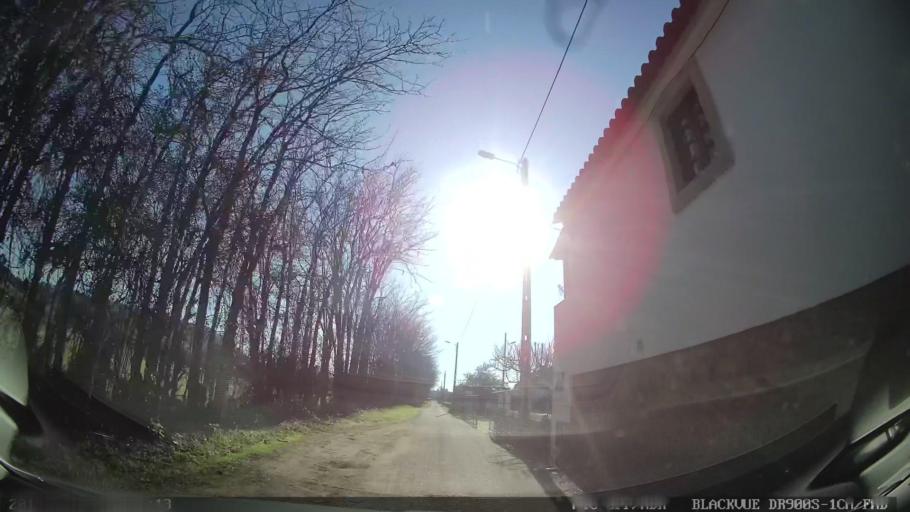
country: PT
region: Castelo Branco
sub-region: Idanha-A-Nova
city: Idanha-a-Nova
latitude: 39.9148
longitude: -7.2198
